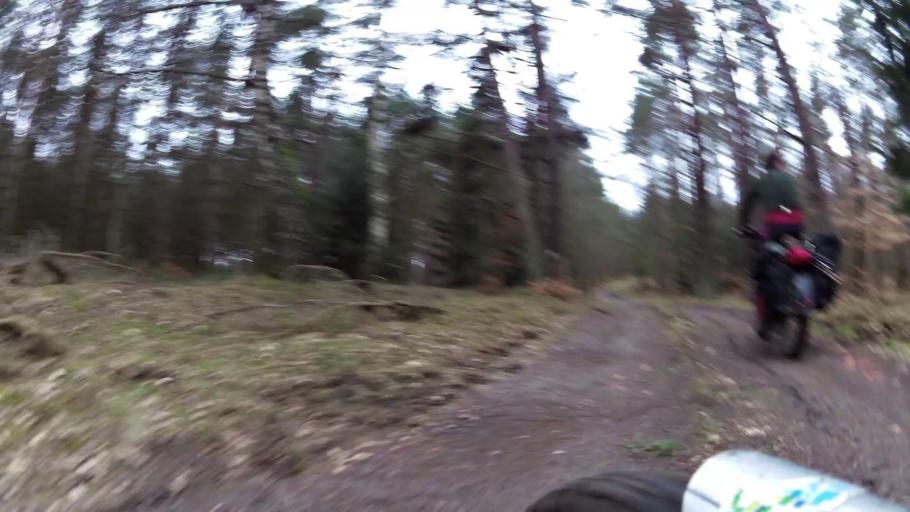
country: PL
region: Pomeranian Voivodeship
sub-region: Powiat bytowski
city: Trzebielino
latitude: 54.1350
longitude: 17.1441
